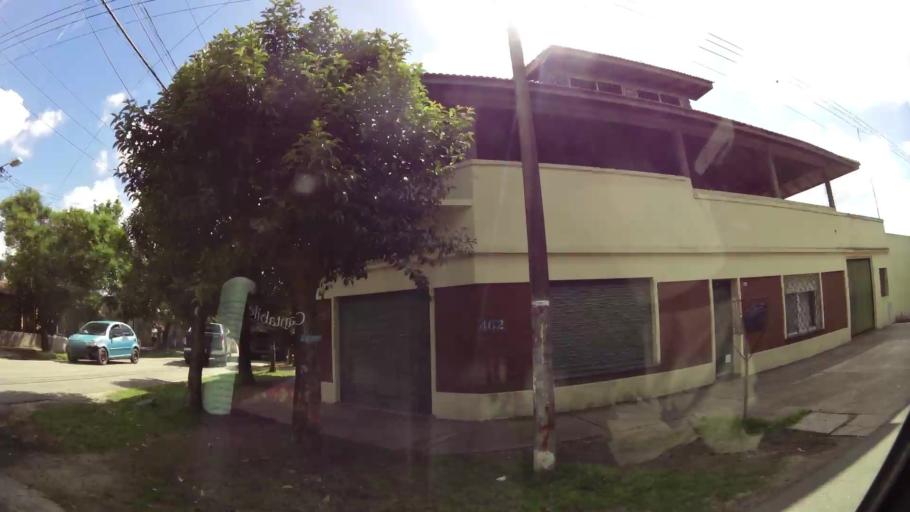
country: AR
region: Buenos Aires
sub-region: Partido de Quilmes
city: Quilmes
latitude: -34.8317
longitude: -58.1761
